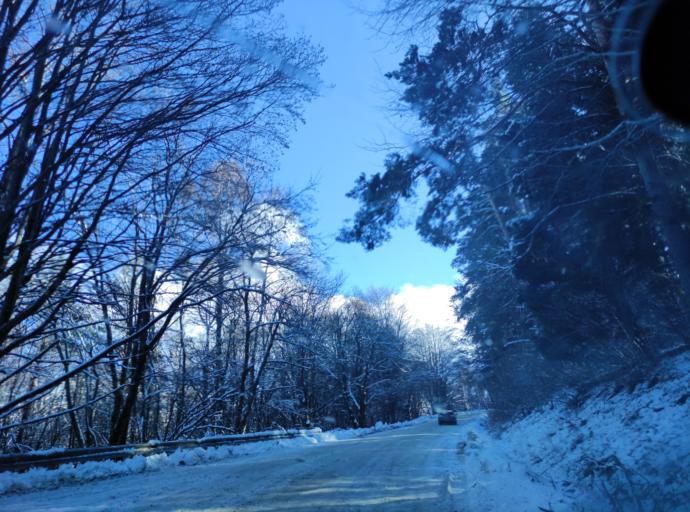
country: BG
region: Sofia-Capital
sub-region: Stolichna Obshtina
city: Sofia
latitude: 42.6042
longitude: 23.3008
